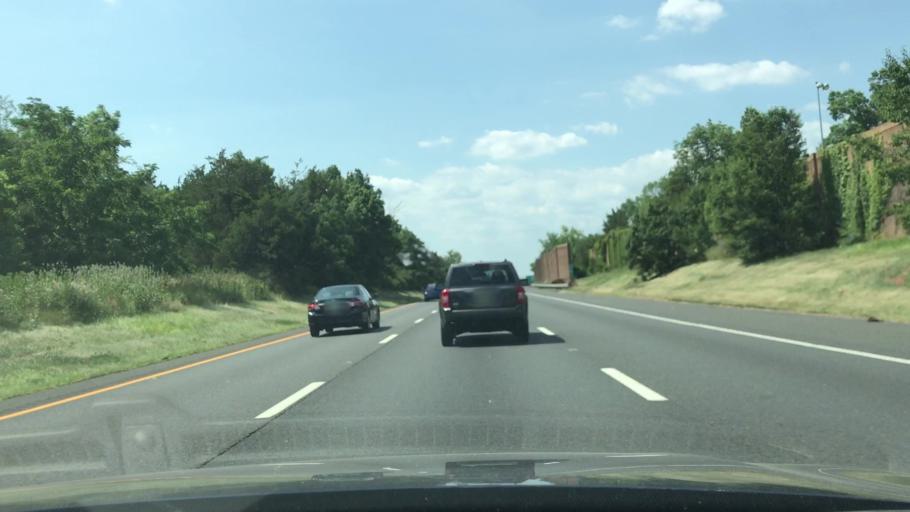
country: US
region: New Jersey
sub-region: Somerset County
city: Green Knoll
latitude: 40.5890
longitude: -74.6171
